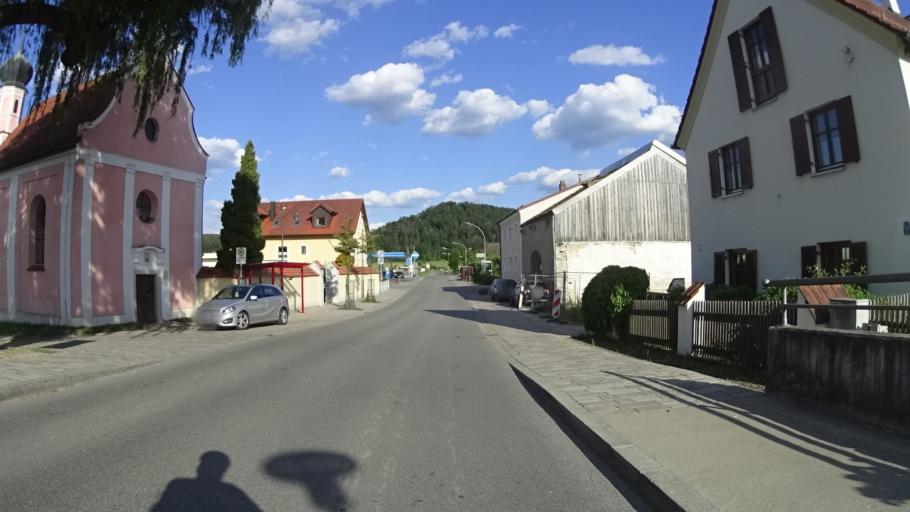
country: DE
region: Bavaria
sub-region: Upper Palatinate
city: Dietfurt
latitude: 49.0338
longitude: 11.5918
